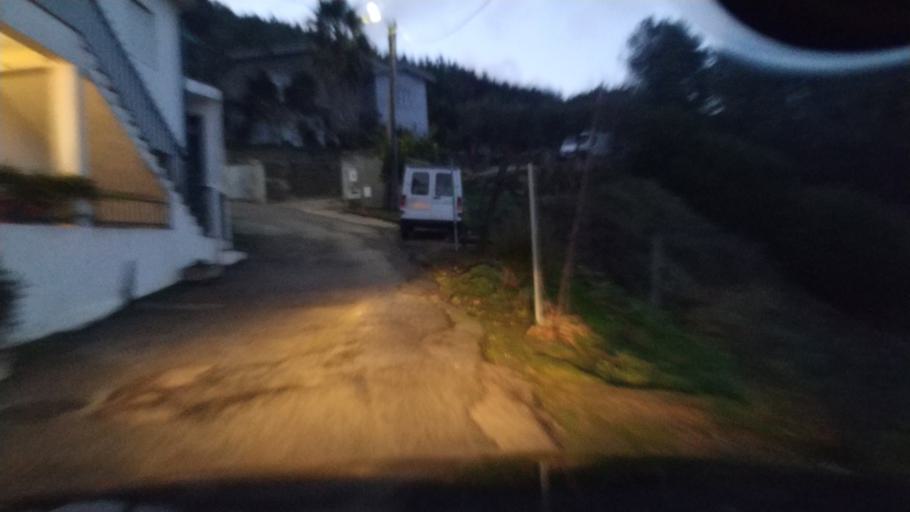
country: PT
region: Vila Real
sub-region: Santa Marta de Penaguiao
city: Santa Marta de Penaguiao
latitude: 41.2567
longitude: -7.7746
